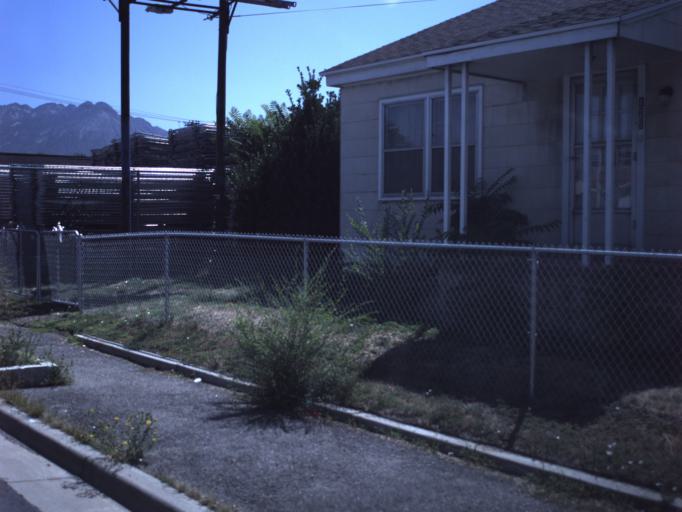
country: US
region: Utah
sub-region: Salt Lake County
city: Centerfield
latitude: 40.6997
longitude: -111.8950
